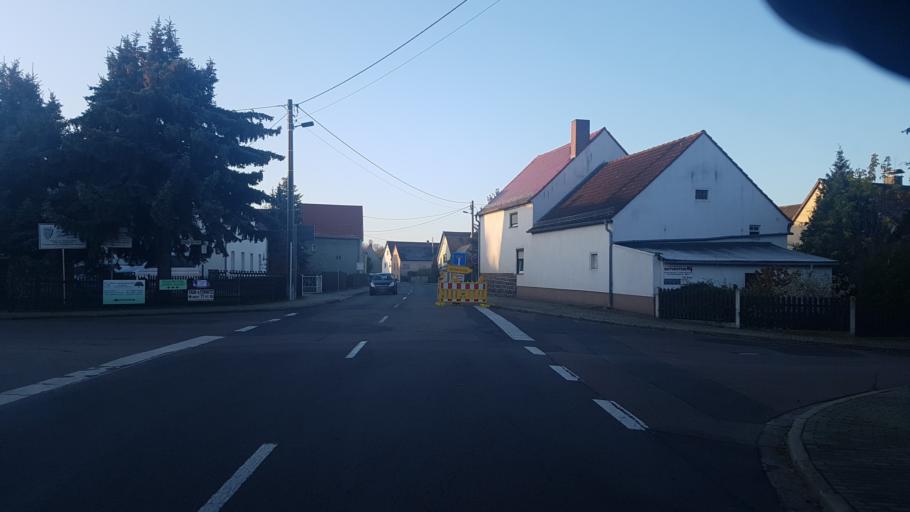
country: DE
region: Saxony
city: Schildau
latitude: 51.4512
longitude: 12.9710
